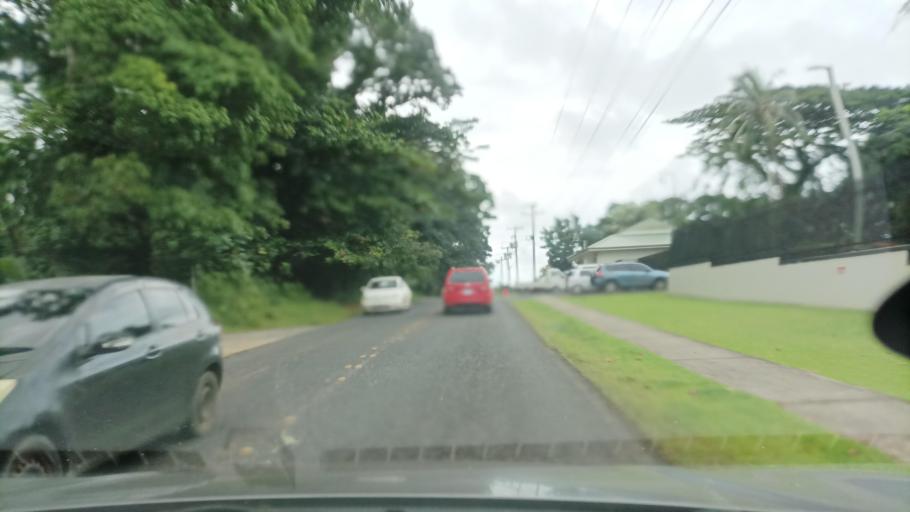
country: FM
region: Pohnpei
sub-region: Kolonia Municipality
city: Kolonia
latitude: 6.9572
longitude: 158.2160
